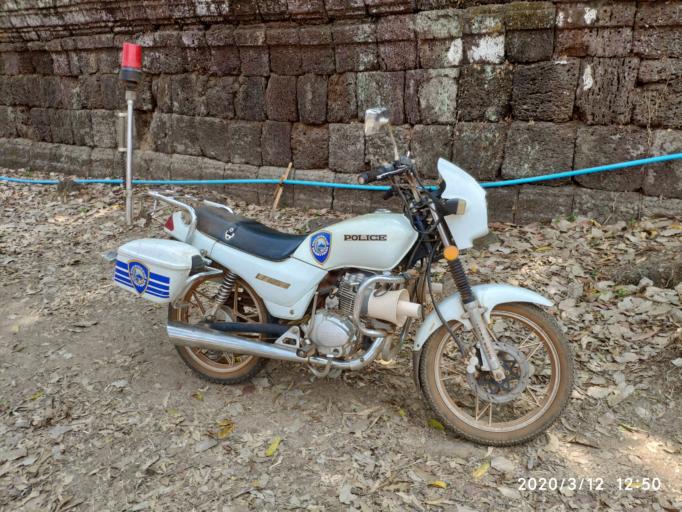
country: KH
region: Preah Vihear
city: Tbeng Meanchey
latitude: 13.7841
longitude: 104.5384
